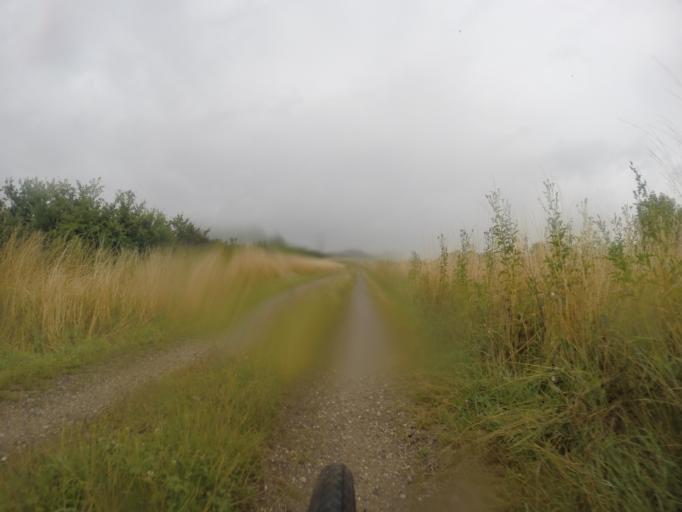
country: DK
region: Capital Region
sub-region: Hoje-Taastrup Kommune
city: Taastrup
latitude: 55.6882
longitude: 12.3117
